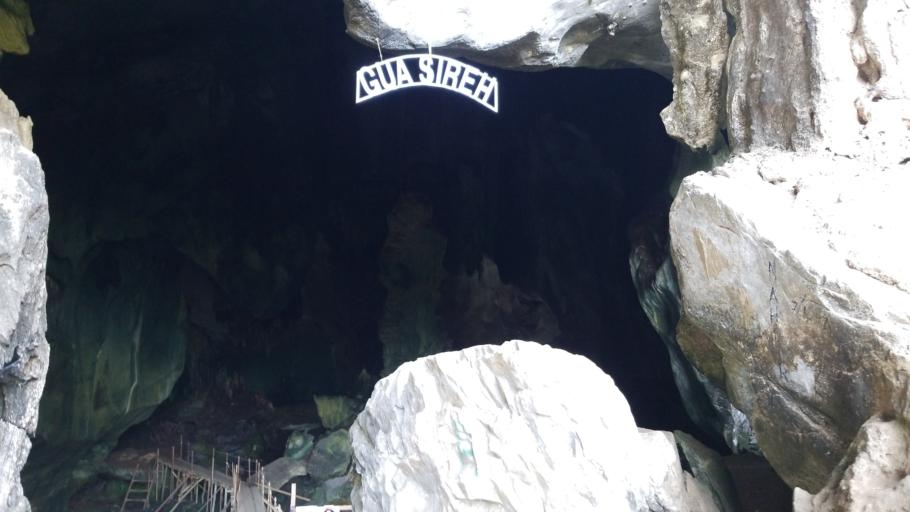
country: TH
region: Yala
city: Betong
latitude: 5.6828
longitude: 100.8891
